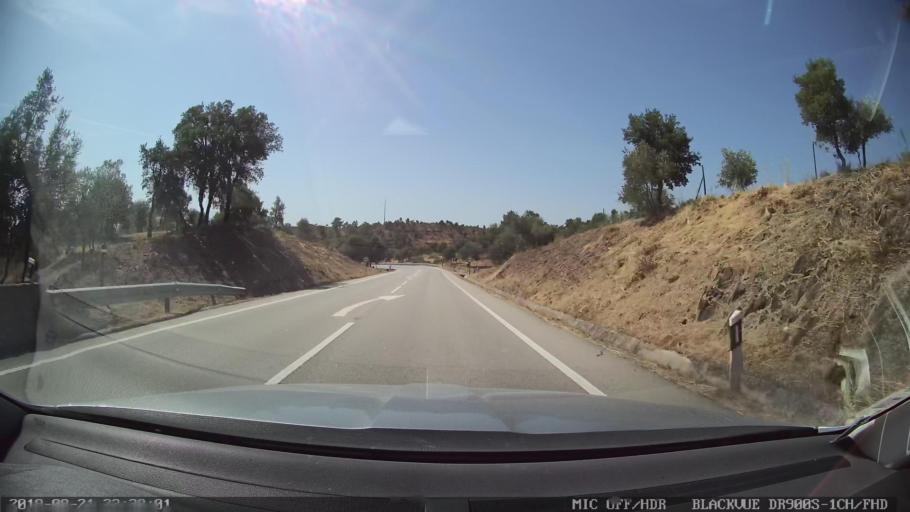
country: PT
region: Guarda
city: Alcains
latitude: 39.8630
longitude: -7.3555
